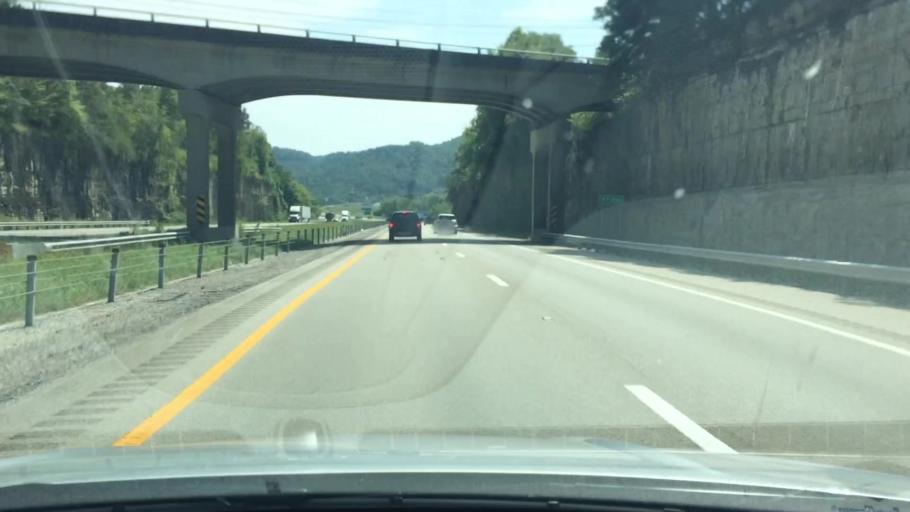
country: US
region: Kentucky
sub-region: Whitley County
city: Williamsburg
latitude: 36.7335
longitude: -84.1724
